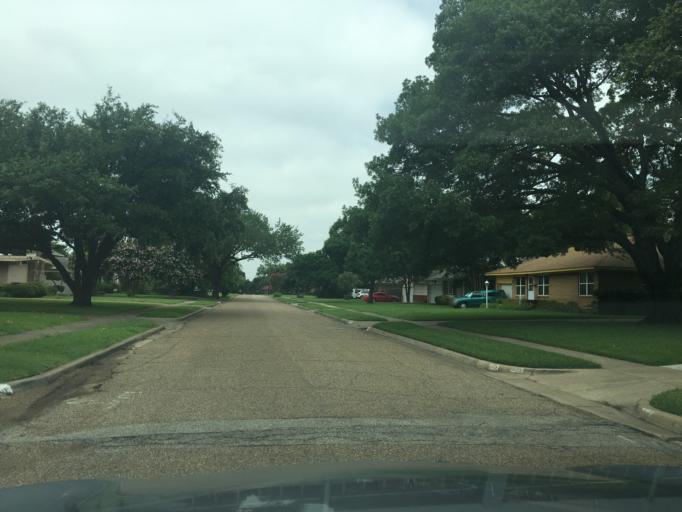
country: US
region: Texas
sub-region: Dallas County
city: Richardson
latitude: 32.9490
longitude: -96.7401
